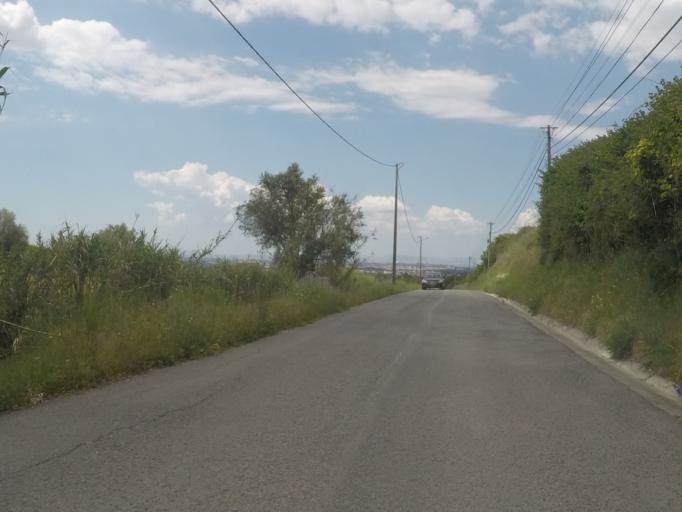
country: PT
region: Setubal
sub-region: Palmela
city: Quinta do Anjo
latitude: 38.5132
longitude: -9.0067
